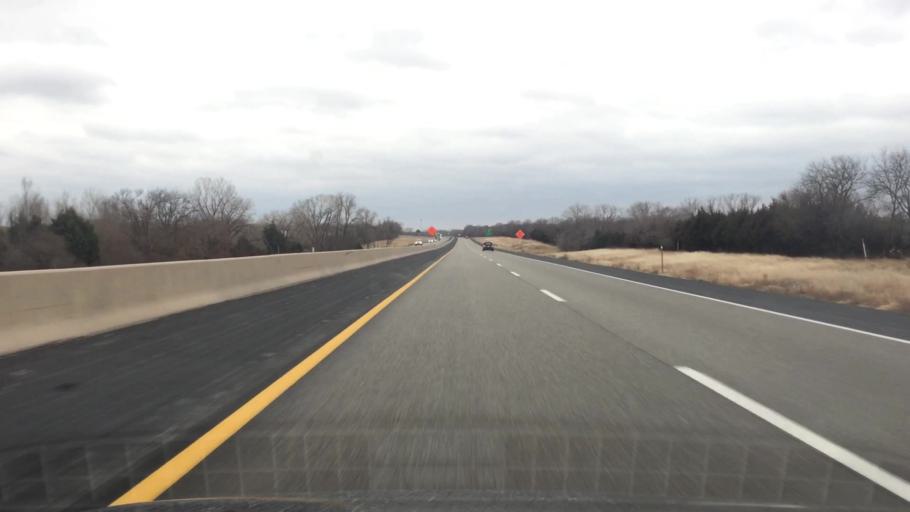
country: US
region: Kansas
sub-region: Butler County
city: Andover
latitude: 37.7008
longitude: -97.1553
